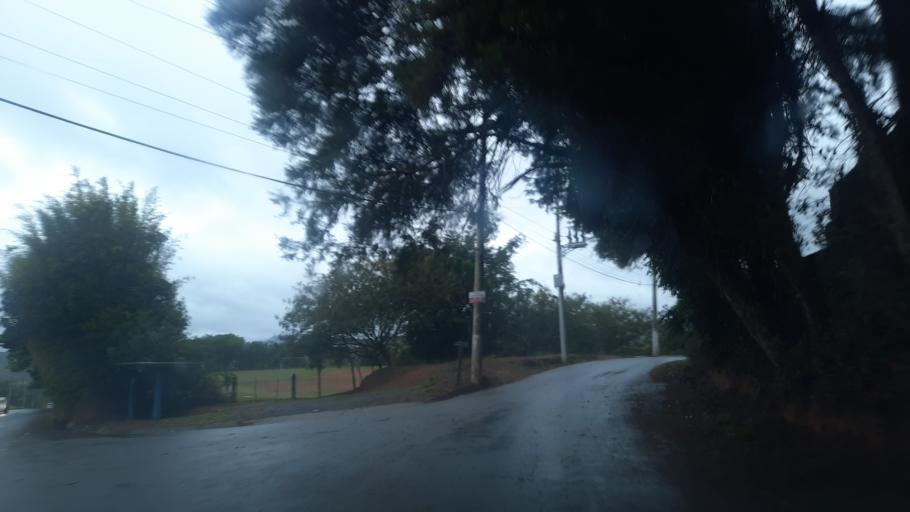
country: BR
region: Sao Paulo
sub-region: Atibaia
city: Atibaia
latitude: -23.0712
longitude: -46.5162
